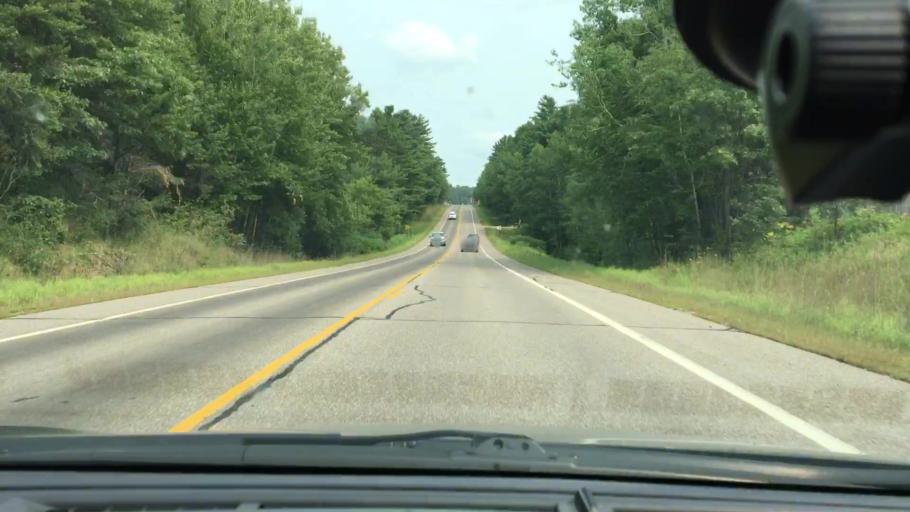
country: US
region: Minnesota
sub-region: Crow Wing County
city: Cross Lake
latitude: 46.7309
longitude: -93.9749
